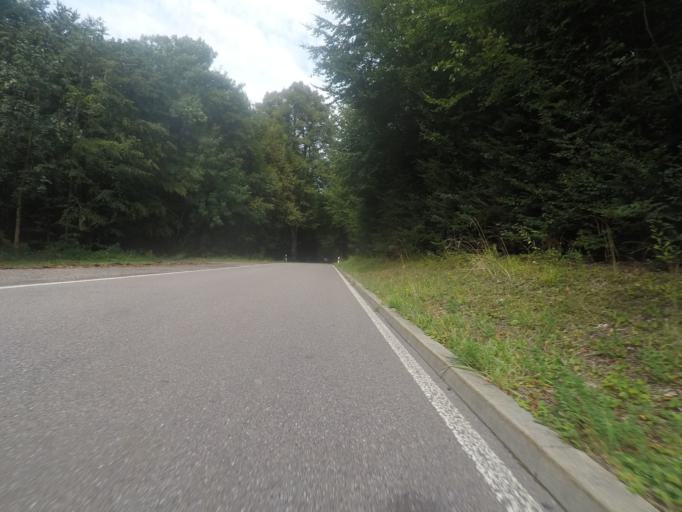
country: DE
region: Baden-Wuerttemberg
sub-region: Karlsruhe Region
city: Bad Herrenalb
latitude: 48.8569
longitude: 8.4075
